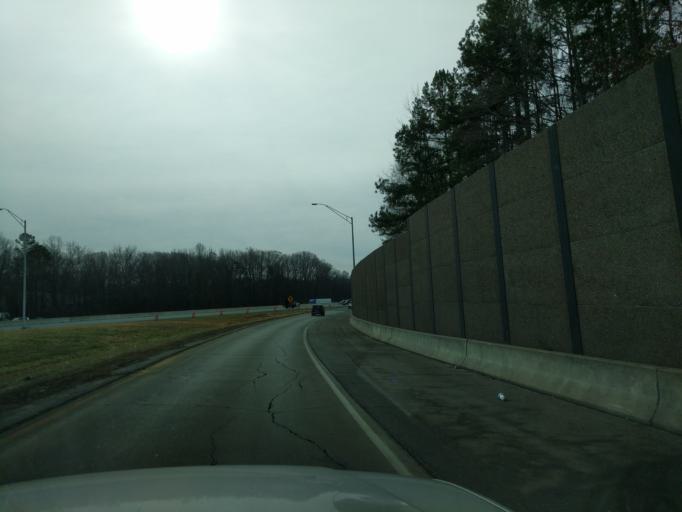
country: US
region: North Carolina
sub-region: Mecklenburg County
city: Charlotte
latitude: 35.3055
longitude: -80.8498
